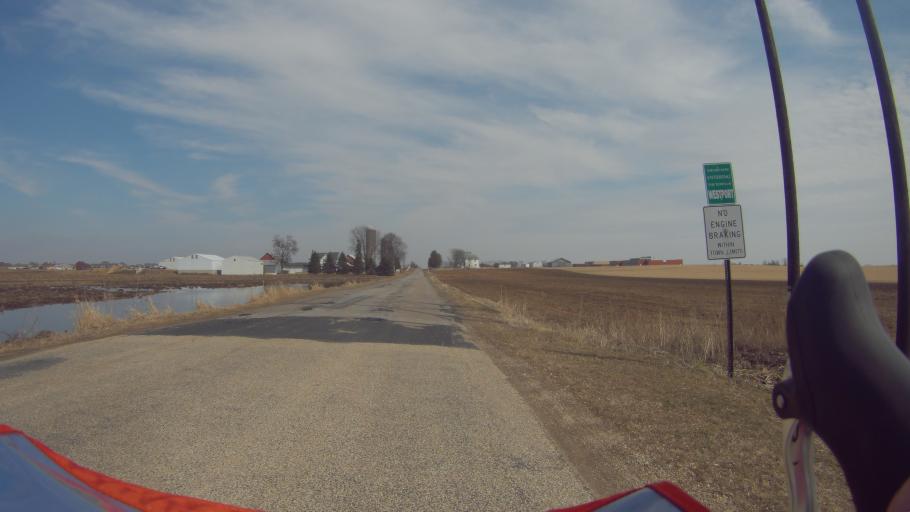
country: US
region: Wisconsin
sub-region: Dane County
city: Waunakee
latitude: 43.1775
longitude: -89.4816
